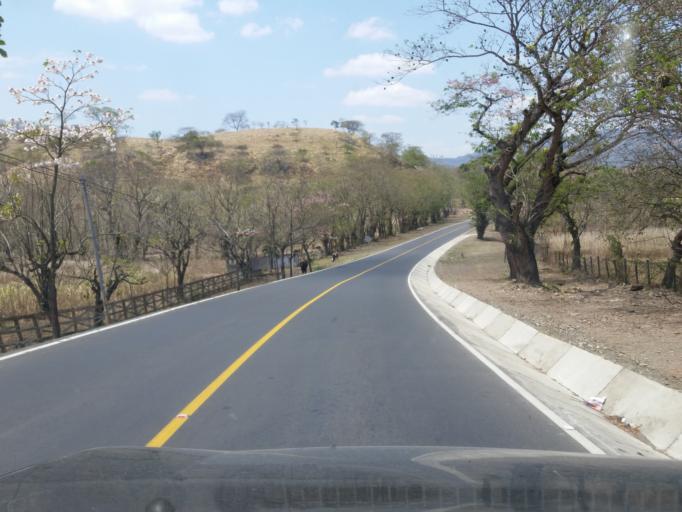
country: NI
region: Boaco
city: Boaco
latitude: 12.4898
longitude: -85.6296
